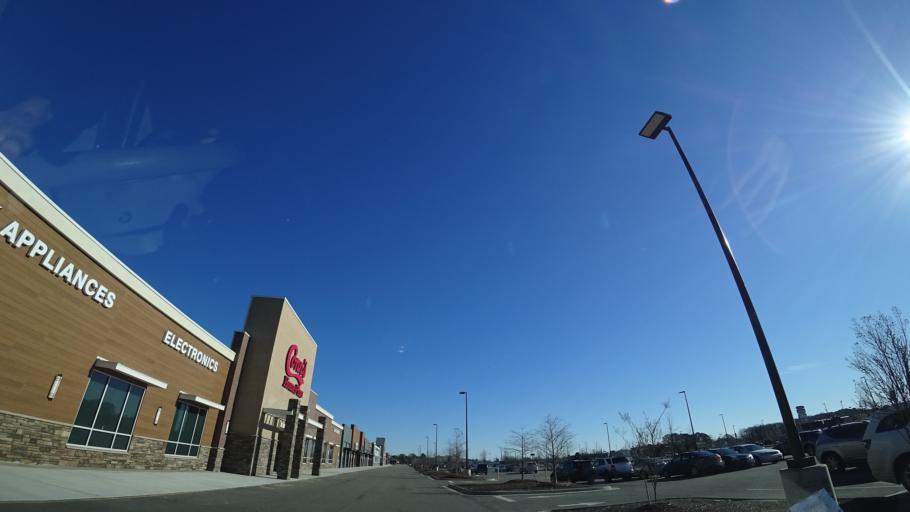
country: US
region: Virginia
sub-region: City of Hampton
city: Hampton
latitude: 37.0438
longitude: -76.3874
